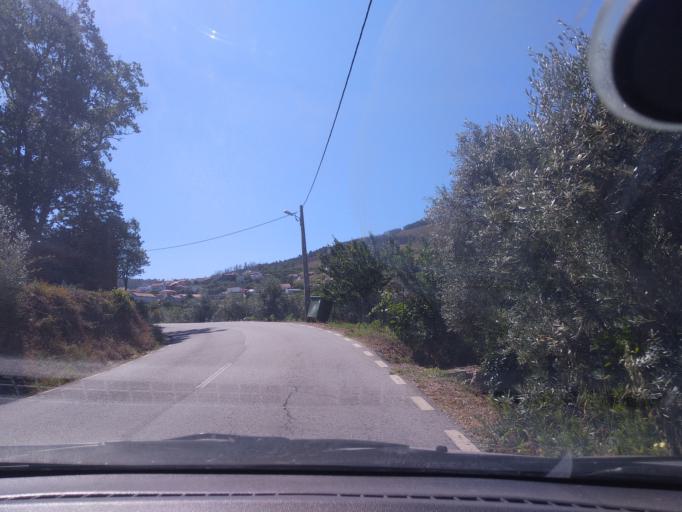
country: PT
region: Castelo Branco
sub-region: Concelho do Fundao
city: Fundao
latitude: 40.1214
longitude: -7.4877
